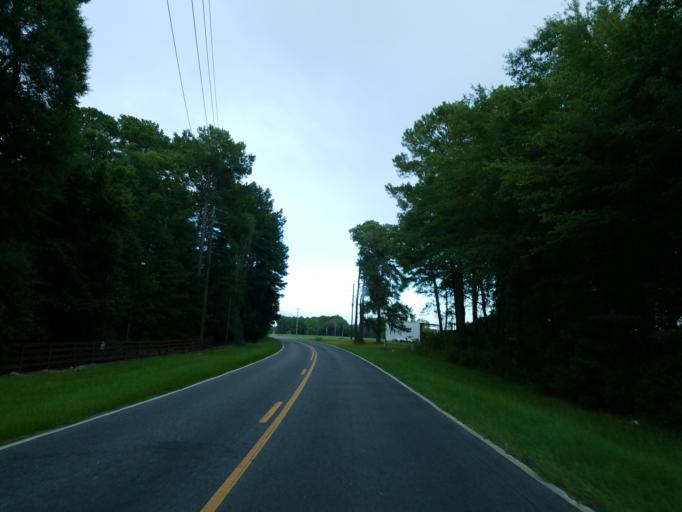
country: US
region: Georgia
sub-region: Cook County
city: Sparks
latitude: 31.2556
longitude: -83.4997
